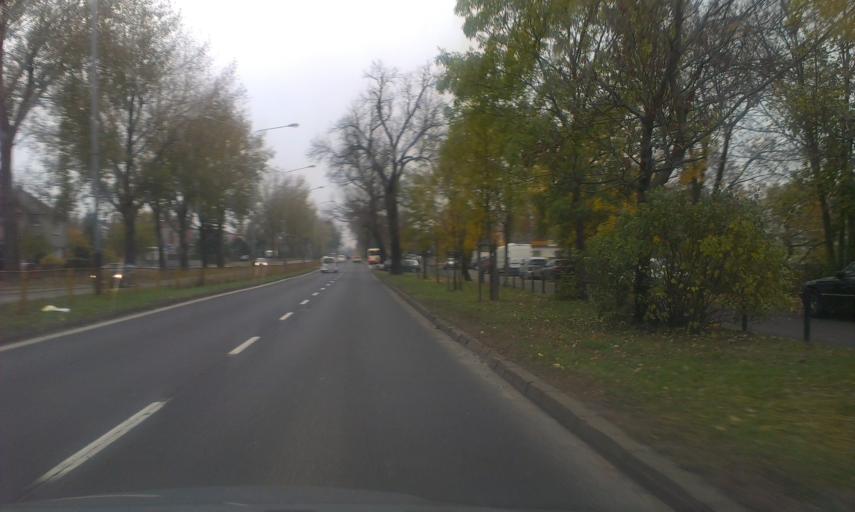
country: PL
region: Greater Poland Voivodeship
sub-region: Powiat poznanski
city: Suchy Las
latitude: 52.4271
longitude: 16.8568
